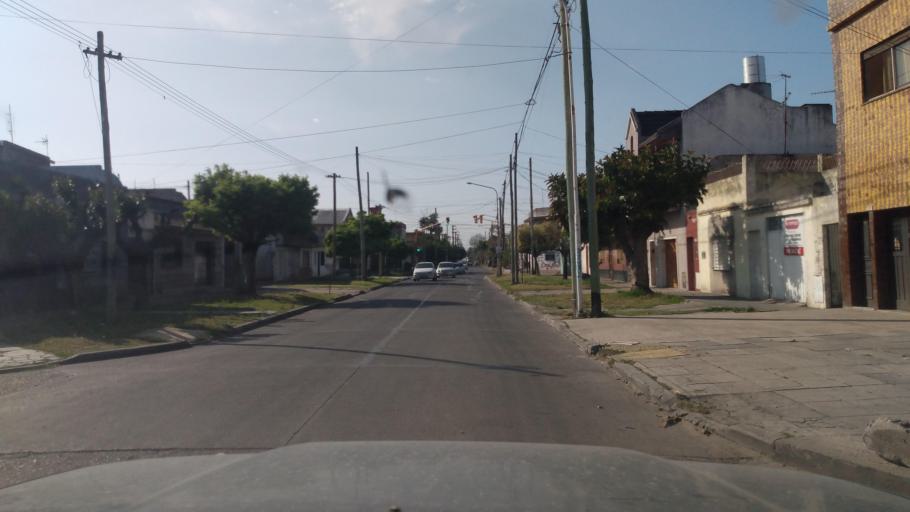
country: AR
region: Buenos Aires
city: San Justo
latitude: -34.6776
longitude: -58.5713
